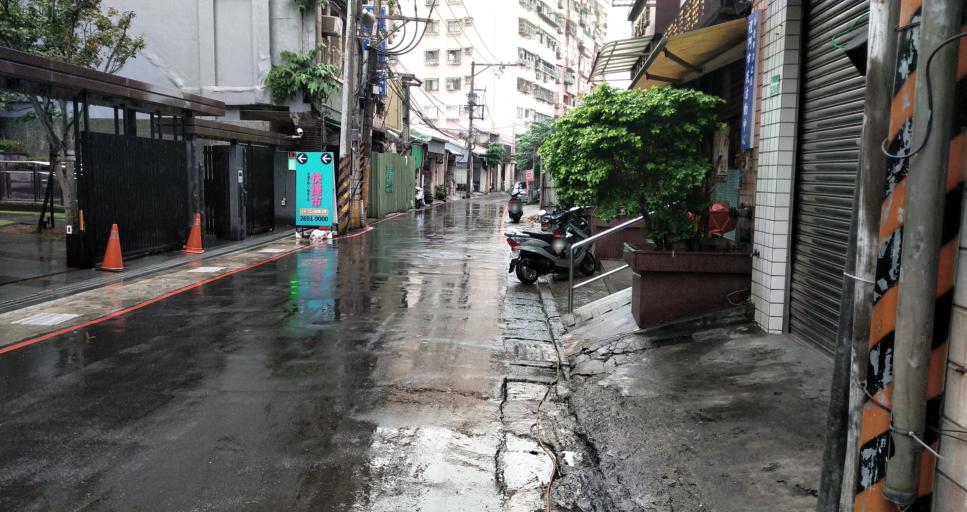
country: TW
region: Taiwan
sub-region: Keelung
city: Keelung
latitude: 25.0681
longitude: 121.6564
